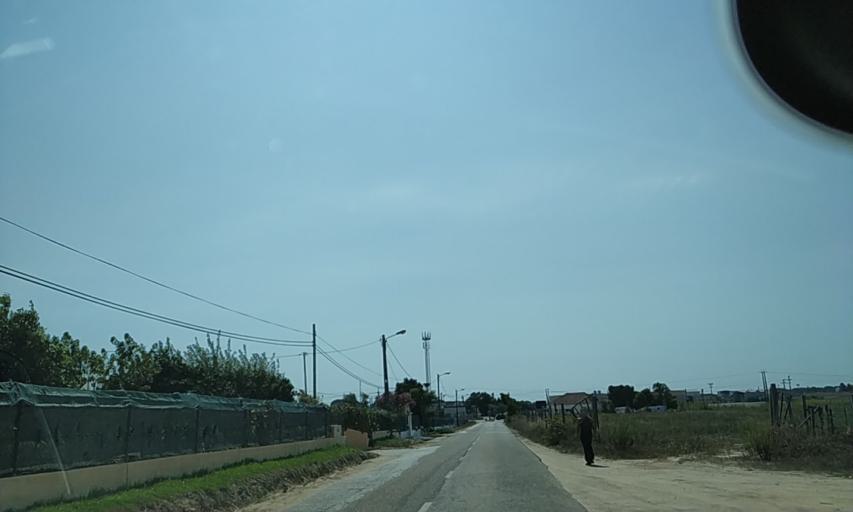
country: PT
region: Santarem
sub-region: Benavente
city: Poceirao
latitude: 38.7495
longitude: -8.6640
